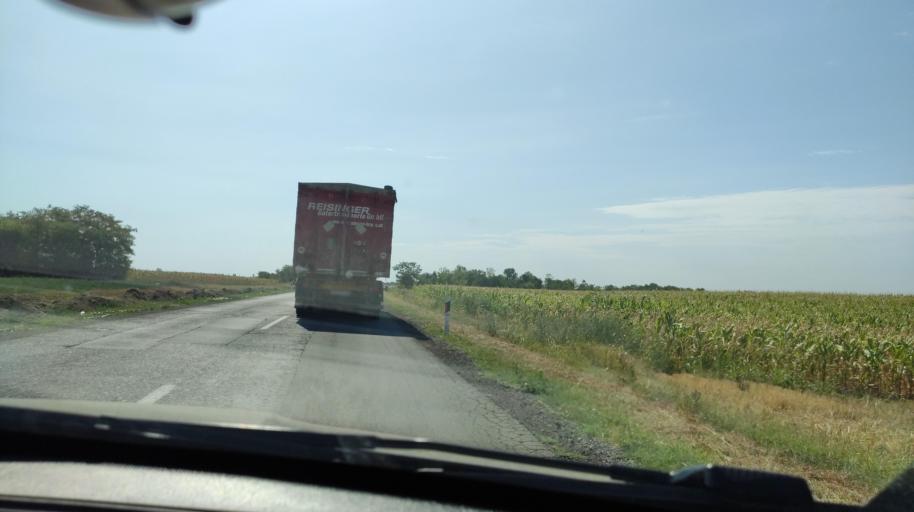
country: RS
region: Autonomna Pokrajina Vojvodina
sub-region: Severnobacki Okrug
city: Backa Topola
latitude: 45.8300
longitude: 19.5939
